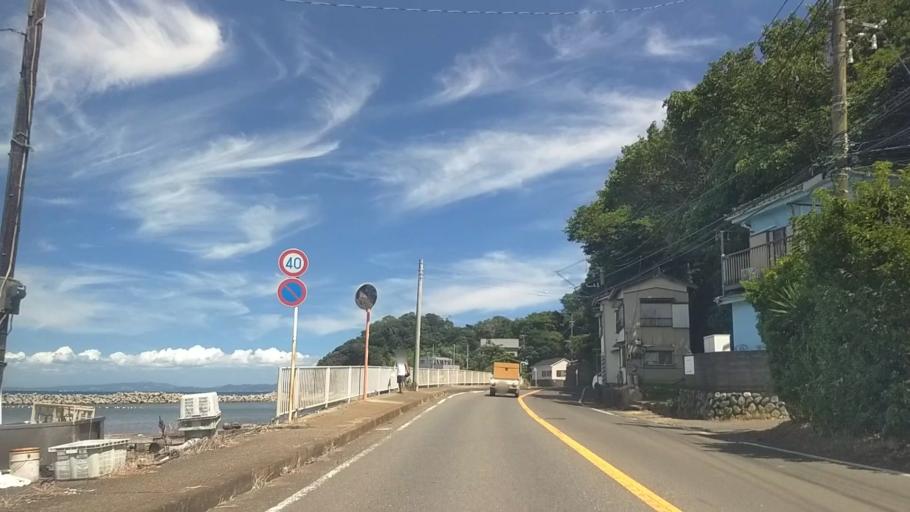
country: JP
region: Kanagawa
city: Miura
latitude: 35.1576
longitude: 139.6674
